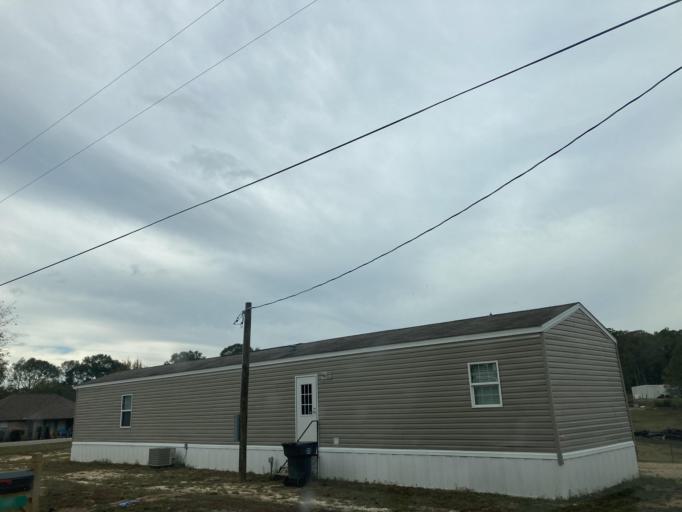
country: US
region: Mississippi
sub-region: Lamar County
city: Purvis
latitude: 31.1193
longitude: -89.4602
